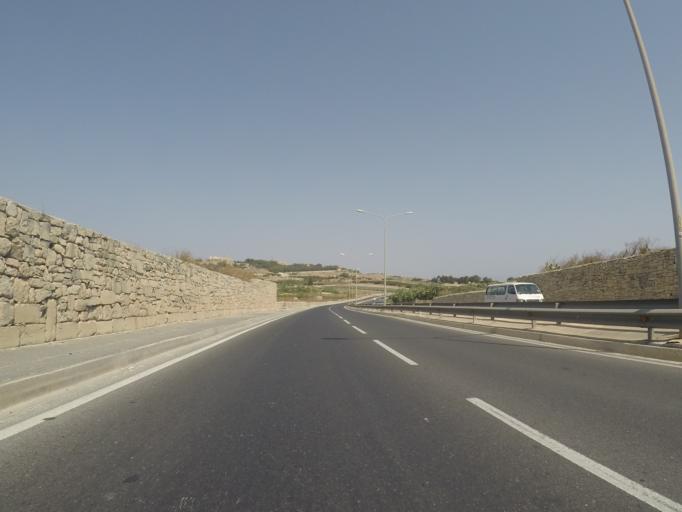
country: MT
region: L-Imdina
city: Imdina
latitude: 35.8850
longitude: 14.4120
